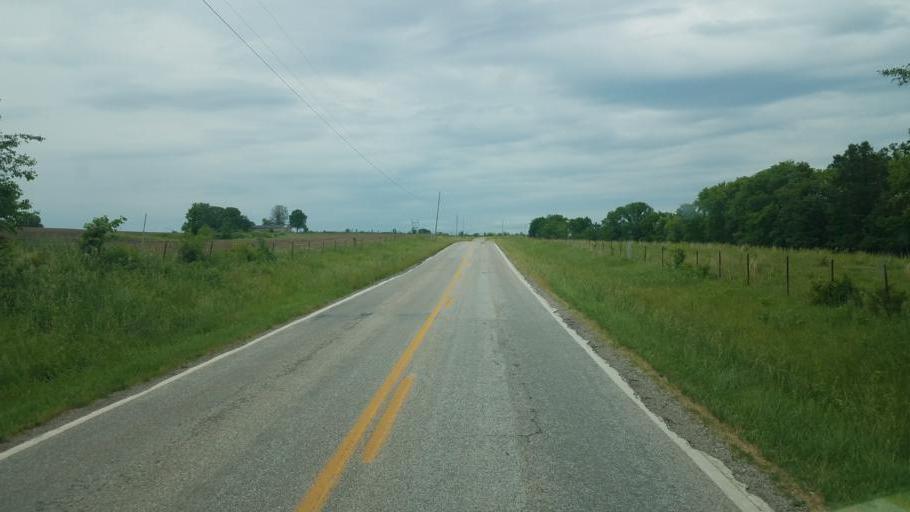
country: US
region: Missouri
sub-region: Moniteau County
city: California
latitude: 38.6680
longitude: -92.5849
